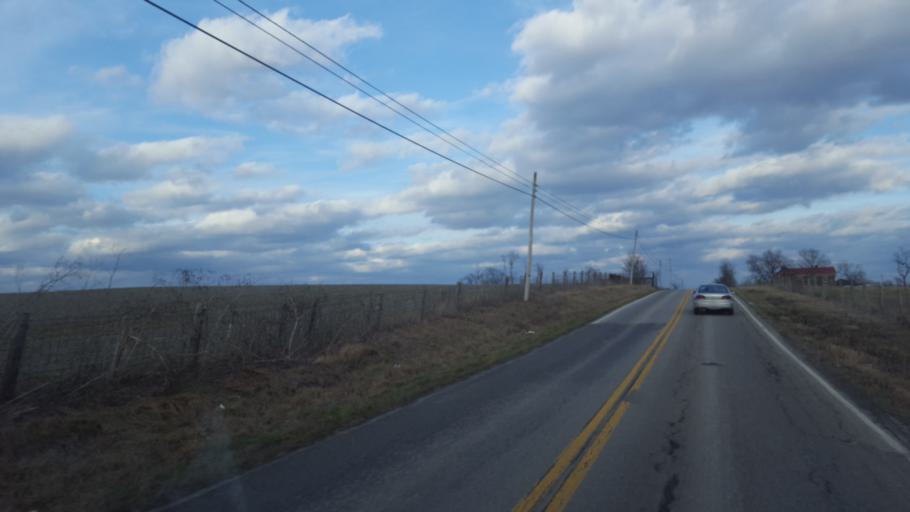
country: US
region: Kentucky
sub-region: Fleming County
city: Flemingsburg
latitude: 38.4776
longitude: -83.6576
